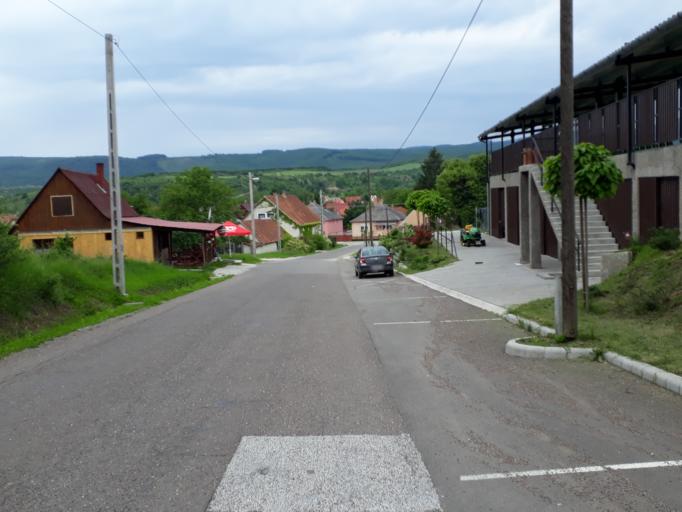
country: HU
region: Heves
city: Felsotarkany
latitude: 47.9772
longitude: 20.4299
